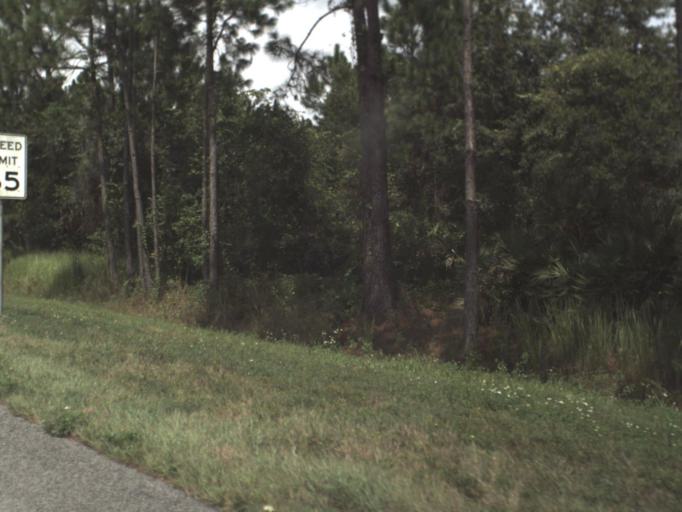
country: US
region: Florida
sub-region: Polk County
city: Frostproof
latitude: 27.7573
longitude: -81.5891
